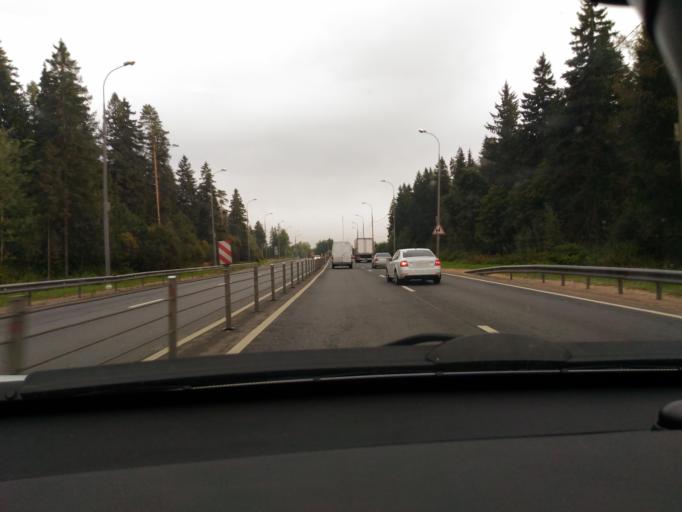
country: RU
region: Moskovskaya
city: Nekrasovskiy
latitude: 56.1114
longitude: 37.5224
